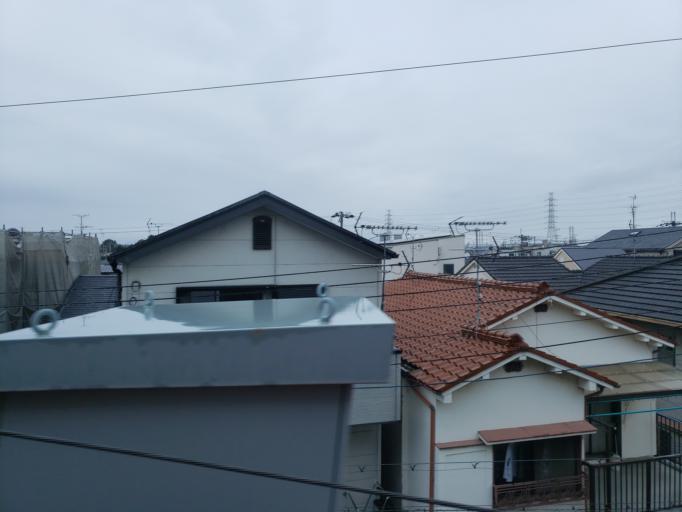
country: JP
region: Hyogo
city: Amagasaki
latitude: 34.7177
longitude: 135.3854
